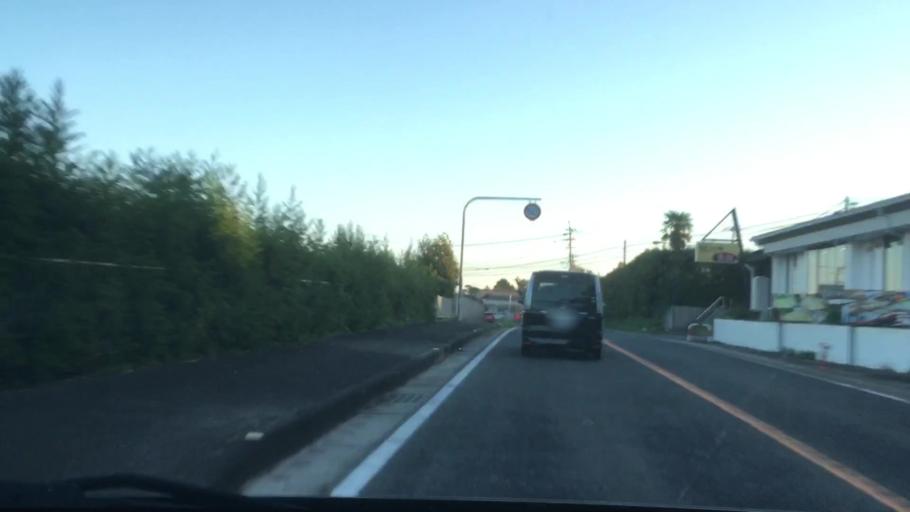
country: JP
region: Nagasaki
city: Sasebo
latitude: 33.0729
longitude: 129.7607
